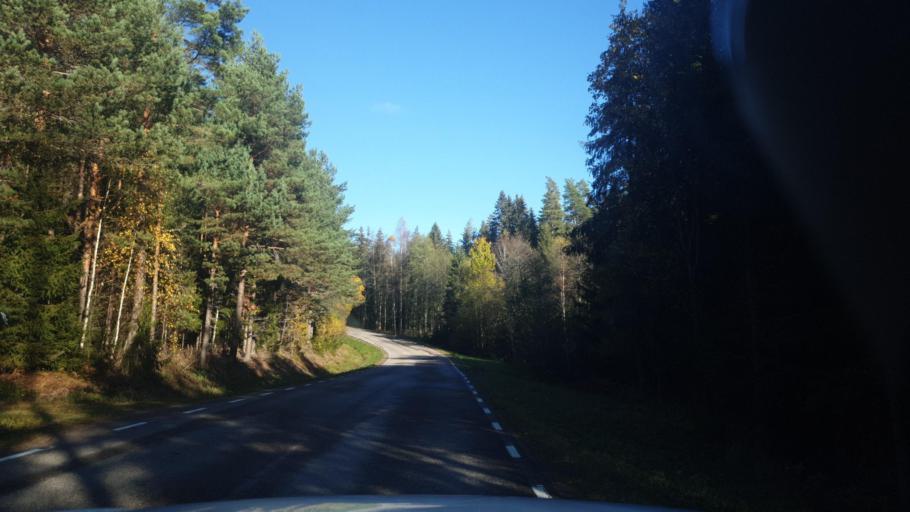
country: SE
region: Vaermland
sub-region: Arvika Kommun
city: Arvika
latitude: 59.6115
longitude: 12.7796
